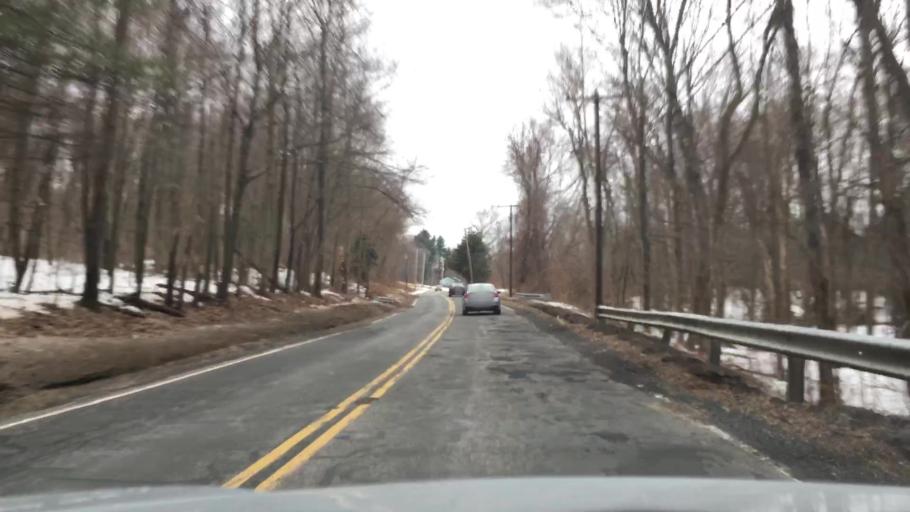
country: US
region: Massachusetts
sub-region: Hampden County
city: Southwick
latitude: 42.0727
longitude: -72.7234
